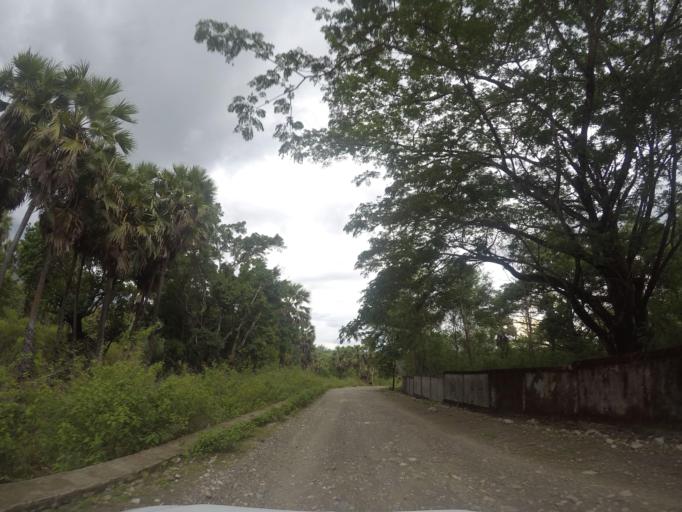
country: TL
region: Bobonaro
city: Maliana
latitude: -8.9746
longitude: 125.2255
